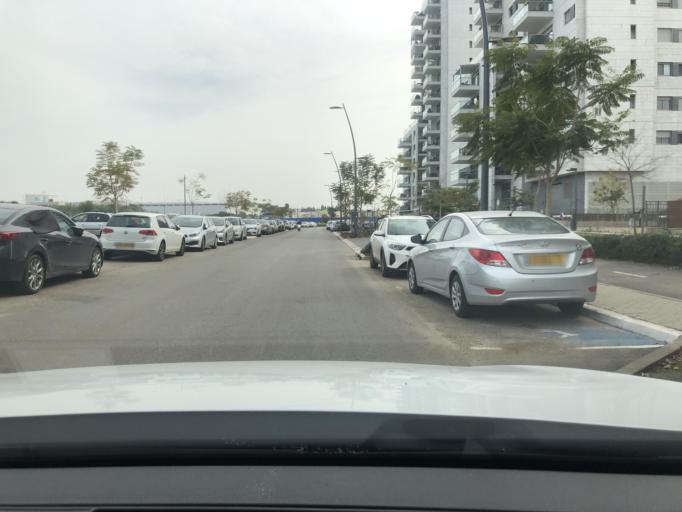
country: IL
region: Central District
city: Rosh Ha'Ayin
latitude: 32.1072
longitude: 34.9469
